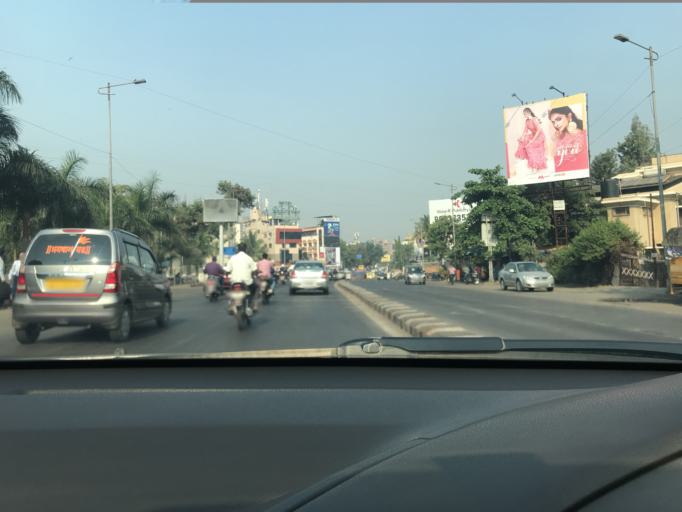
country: IN
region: Maharashtra
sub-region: Pune Division
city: Khadki
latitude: 18.5513
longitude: 73.8047
